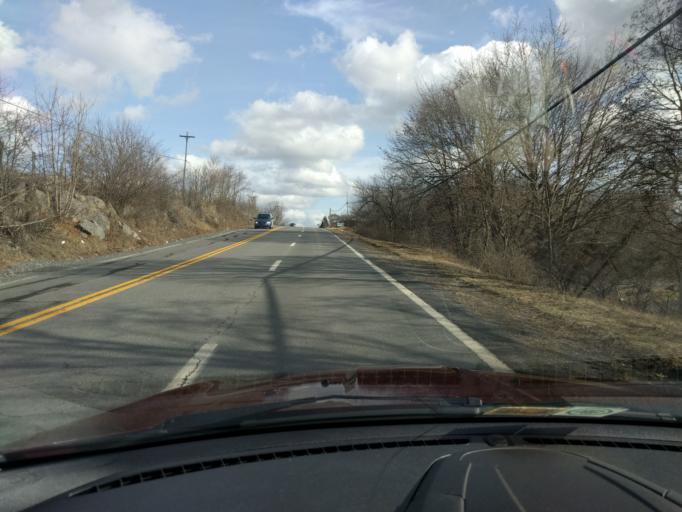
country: US
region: West Virginia
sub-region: Greenbrier County
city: Lewisburg
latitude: 37.8058
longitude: -80.4587
